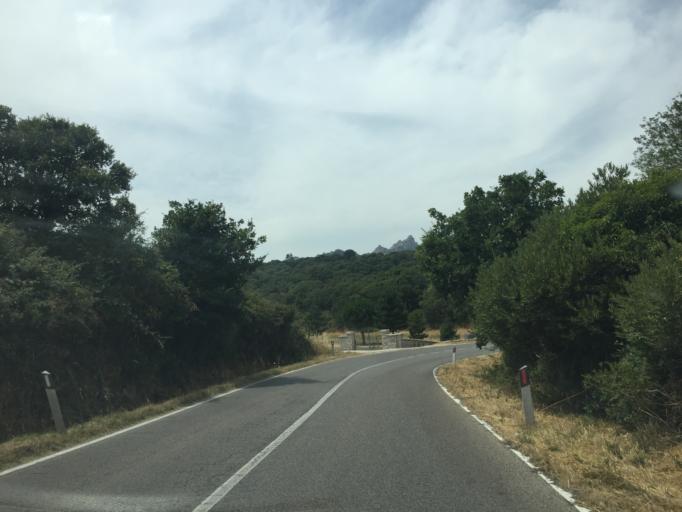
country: IT
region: Sardinia
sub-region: Provincia di Olbia-Tempio
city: Aggius
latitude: 40.9151
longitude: 9.0731
